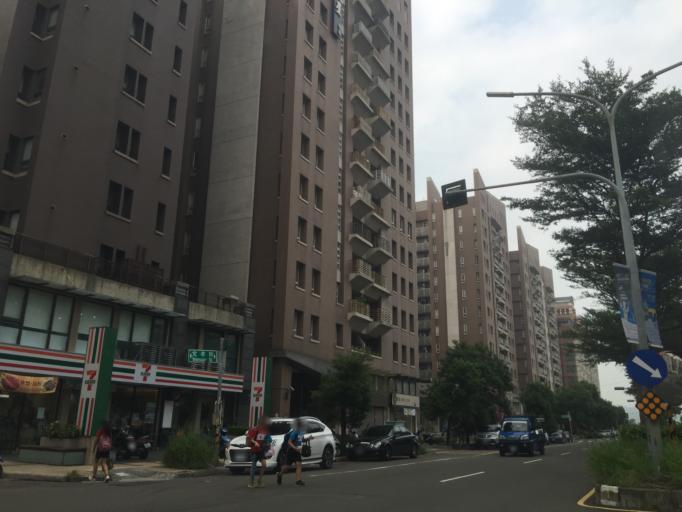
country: TW
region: Taiwan
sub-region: Hsinchu
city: Zhubei
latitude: 24.8328
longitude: 121.0189
